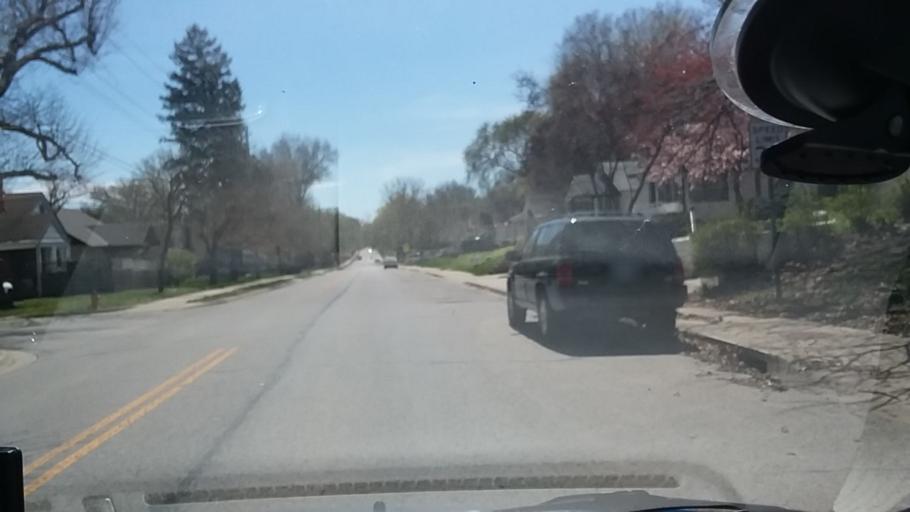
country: US
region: Kansas
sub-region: Johnson County
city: Westwood
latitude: 39.0430
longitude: -94.6213
